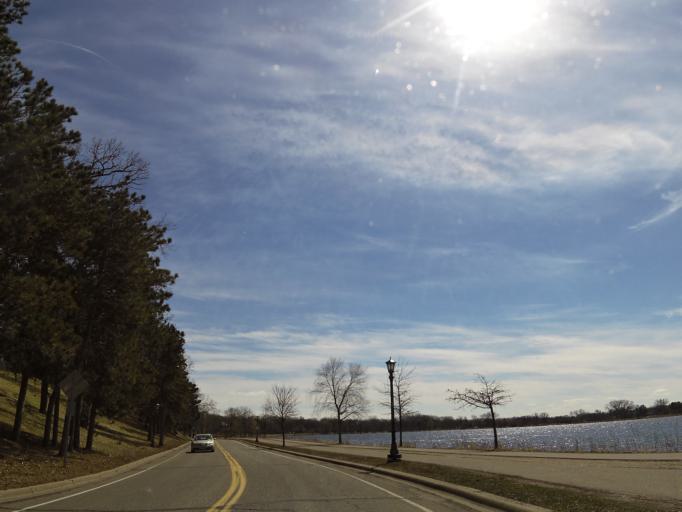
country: US
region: Minnesota
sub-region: Ramsey County
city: Little Canada
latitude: 44.9868
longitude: -93.0512
